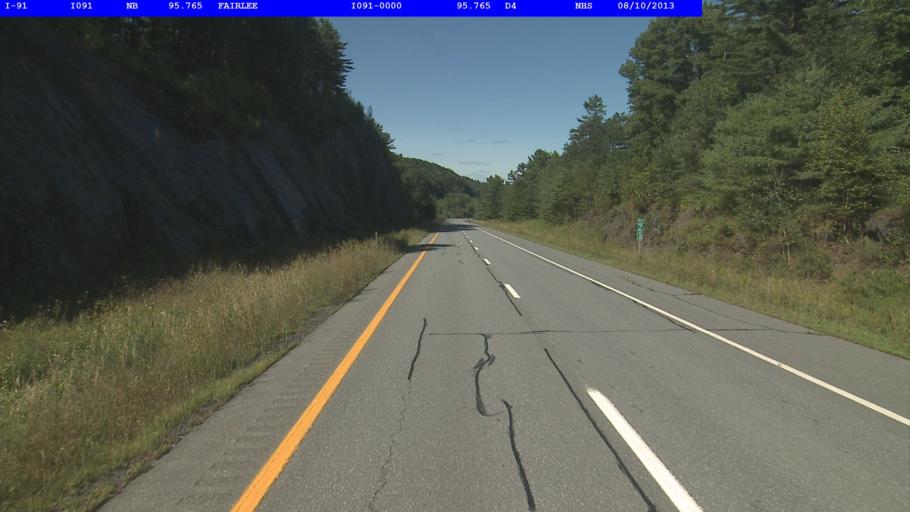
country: US
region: New Hampshire
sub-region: Grafton County
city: Orford
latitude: 43.9584
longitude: -72.1290
